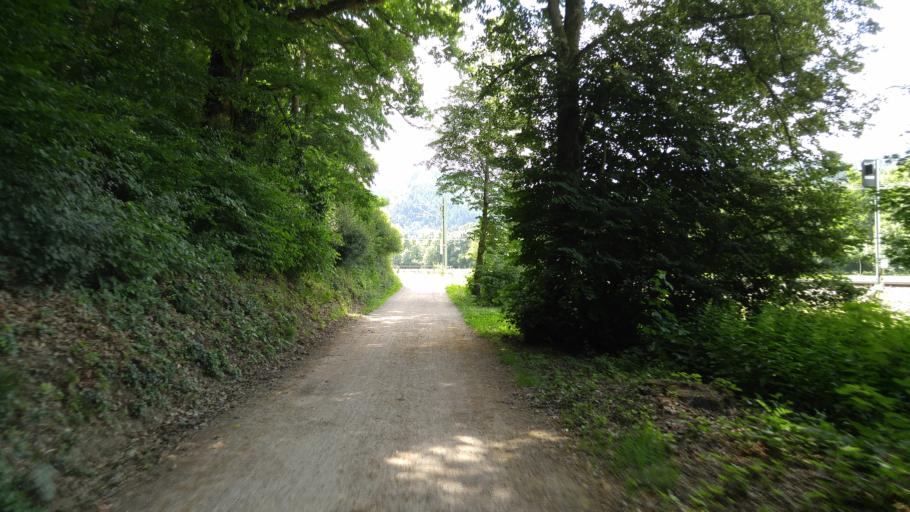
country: DE
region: Baden-Wuerttemberg
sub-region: Freiburg Region
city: Muenstertal/Schwarzwald
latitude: 47.8699
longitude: 7.7436
